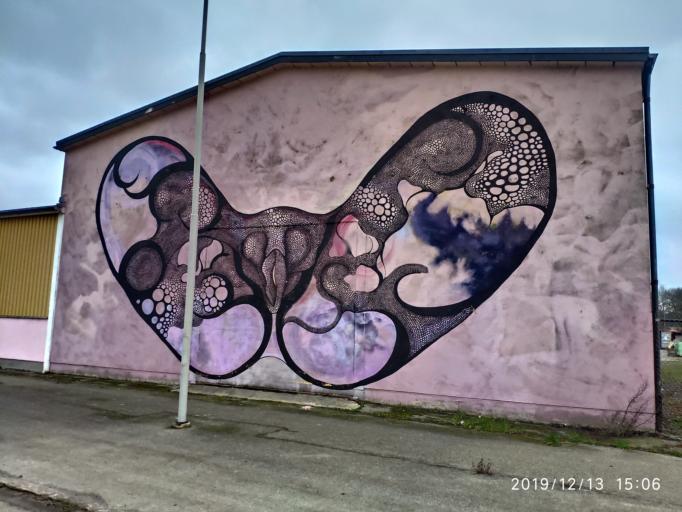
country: SE
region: Skane
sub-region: Ystads Kommun
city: Ystad
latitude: 55.4269
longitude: 13.8407
